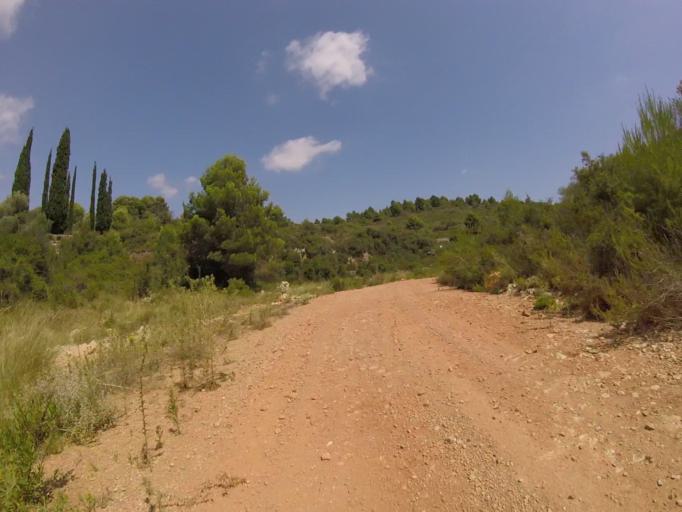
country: ES
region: Valencia
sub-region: Provincia de Castello
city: Torreblanca
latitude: 40.2125
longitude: 0.1391
